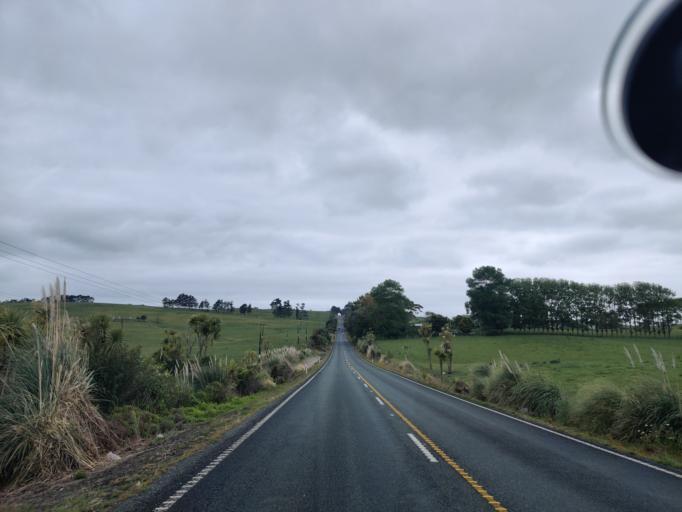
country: NZ
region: Northland
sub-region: Kaipara District
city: Dargaville
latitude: -36.1281
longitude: 174.1232
